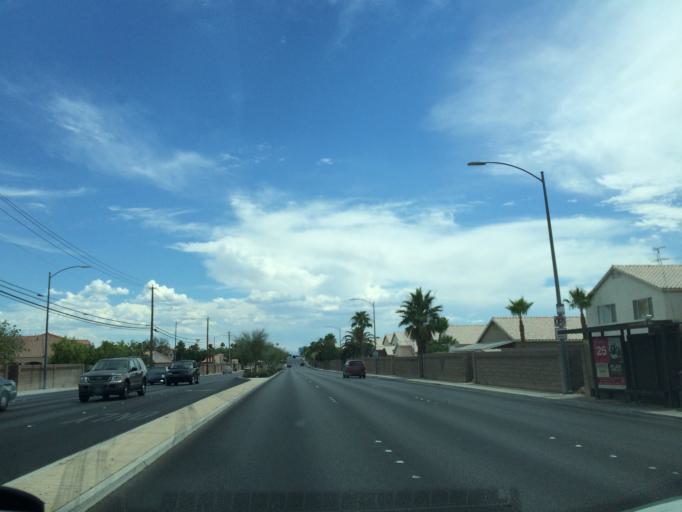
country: US
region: Nevada
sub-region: Clark County
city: North Las Vegas
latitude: 36.2246
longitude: -115.1616
